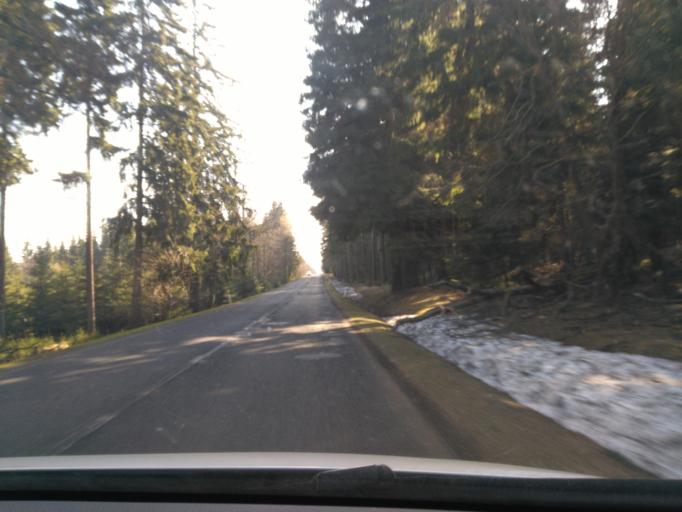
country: CZ
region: Ustecky
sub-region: Okres Chomutov
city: Vejprty
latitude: 50.4884
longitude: 13.0513
